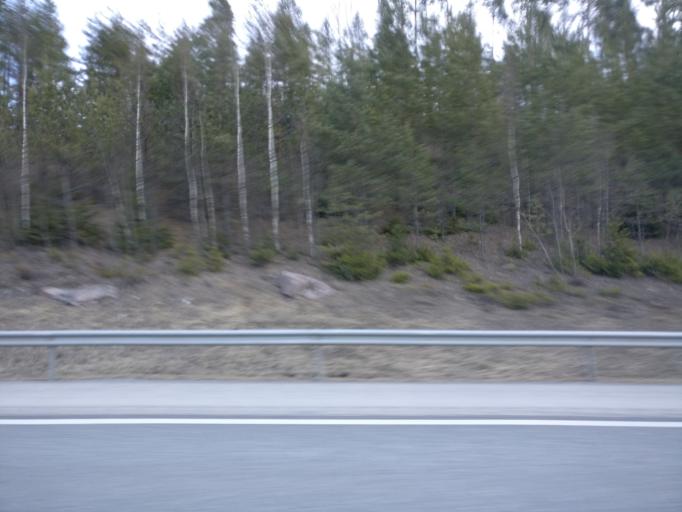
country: FI
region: Haeme
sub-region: Haemeenlinna
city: Janakkala
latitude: 60.8857
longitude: 24.5669
